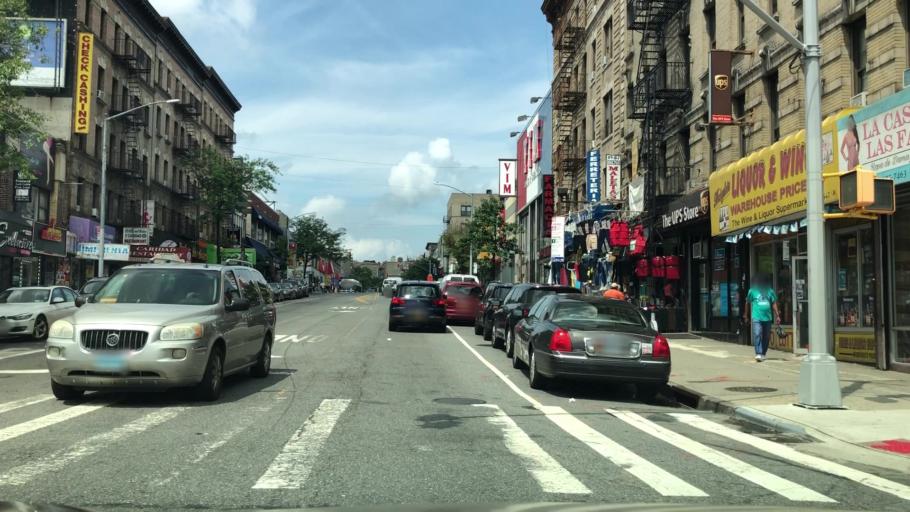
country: US
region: New York
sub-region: New York County
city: Inwood
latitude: 40.8488
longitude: -73.9324
